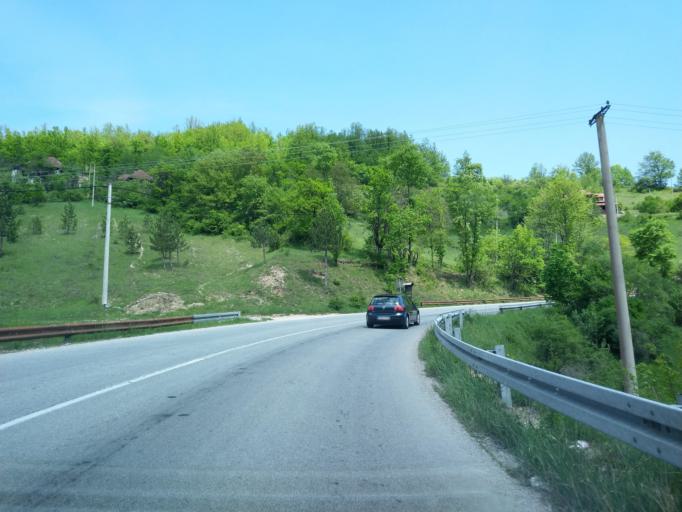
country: RS
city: Durici
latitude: 43.8023
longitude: 19.5049
